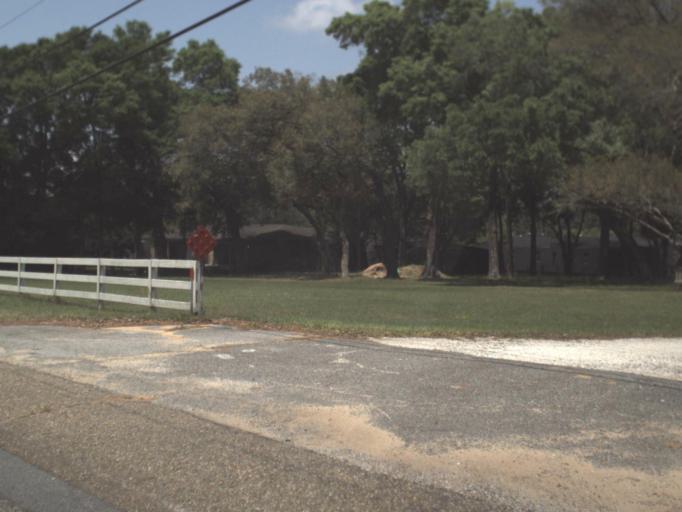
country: US
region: Florida
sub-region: Escambia County
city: Myrtle Grove
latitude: 30.4317
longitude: -87.3000
